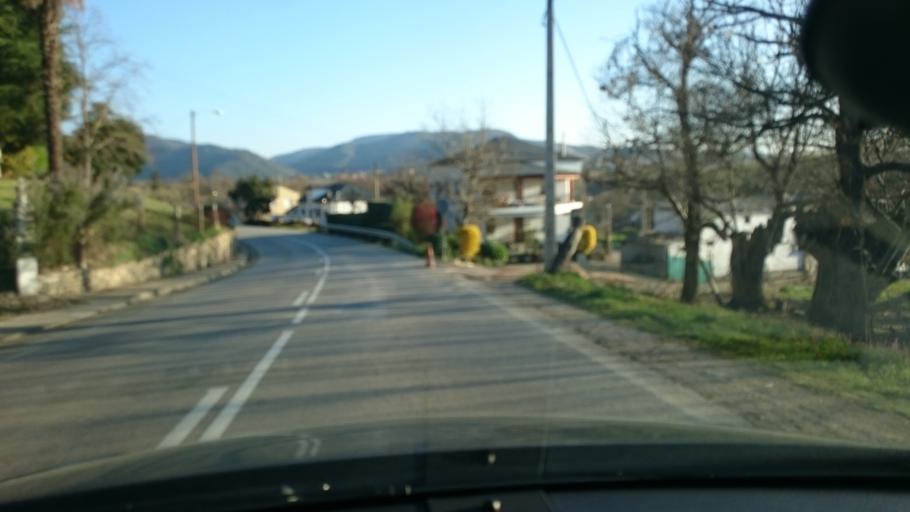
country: ES
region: Castille and Leon
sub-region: Provincia de Leon
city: Corullon
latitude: 42.5857
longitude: -6.8157
